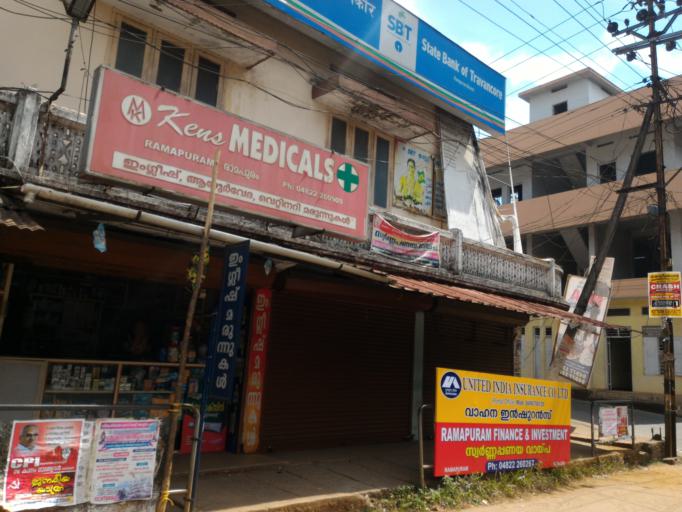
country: IN
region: Kerala
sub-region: Kottayam
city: Palackattumala
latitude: 9.7998
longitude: 76.6625
